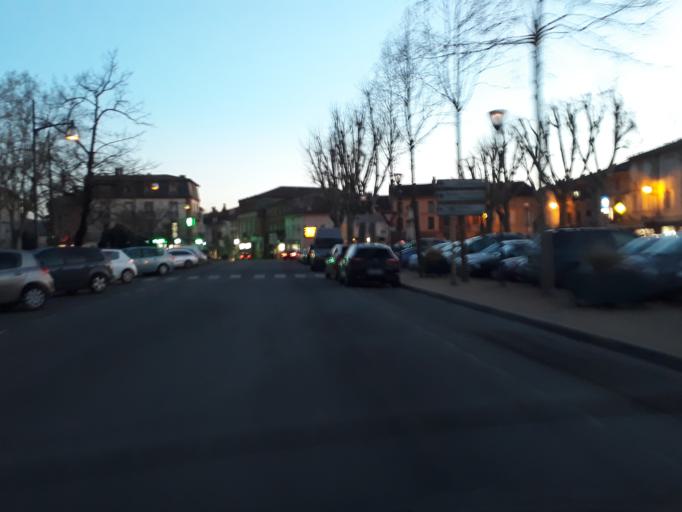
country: FR
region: Midi-Pyrenees
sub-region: Departement de la Haute-Garonne
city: Carbonne
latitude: 43.2967
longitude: 1.2253
